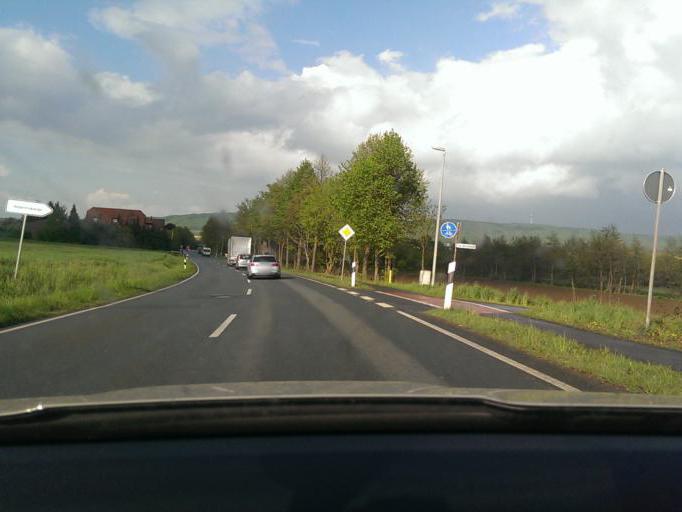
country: DE
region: Lower Saxony
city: Pohle
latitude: 52.2682
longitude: 9.3509
